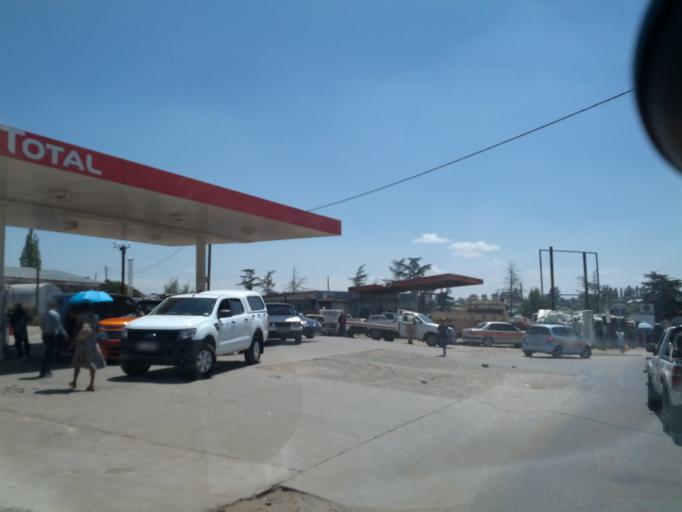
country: LS
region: Butha-Buthe
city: Butha-Buthe
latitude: -28.7684
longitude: 28.2496
